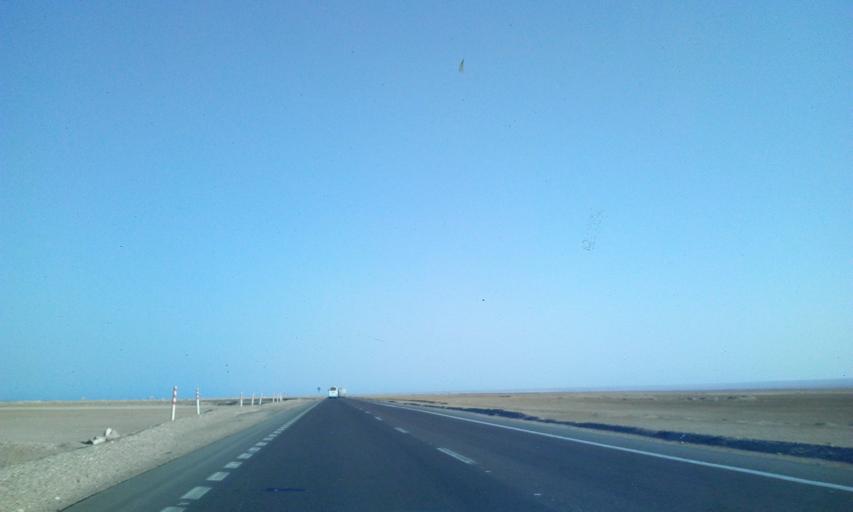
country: EG
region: South Sinai
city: Tor
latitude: 28.6501
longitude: 32.8479
